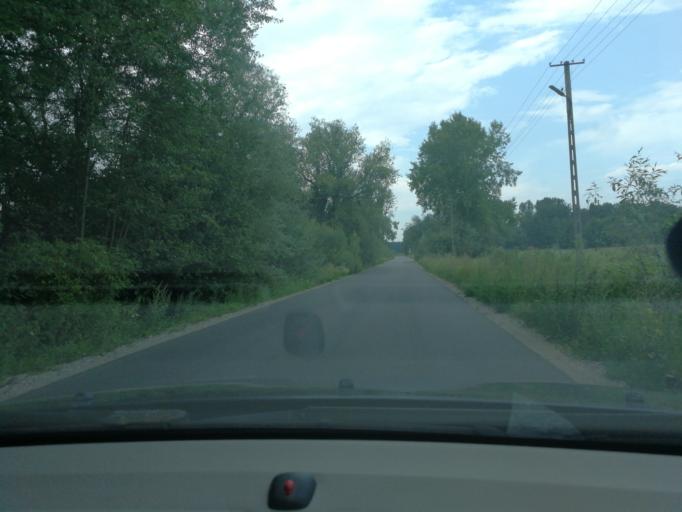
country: PL
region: Masovian Voivodeship
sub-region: Powiat warszawski zachodni
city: Bieniewice
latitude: 52.1097
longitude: 20.5547
